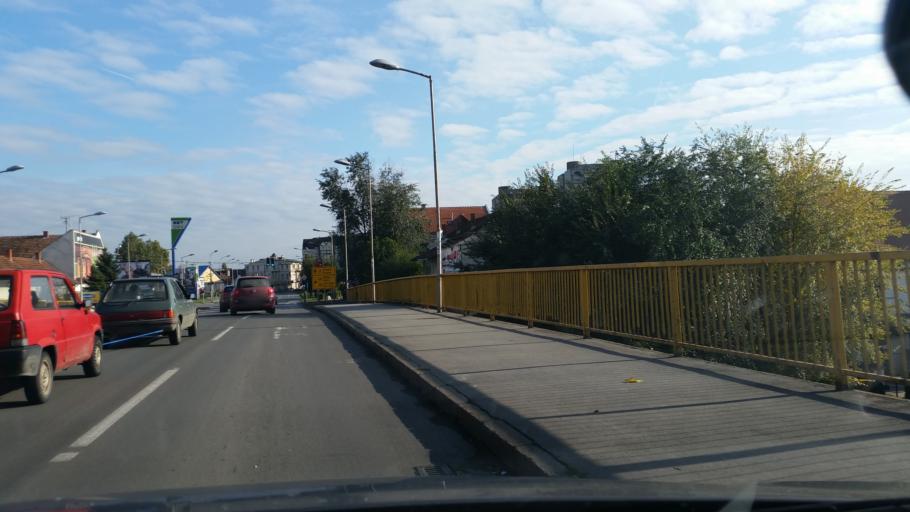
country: RS
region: Autonomna Pokrajina Vojvodina
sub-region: Srednjebanatski Okrug
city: Zrenjanin
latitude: 45.3798
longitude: 20.3982
